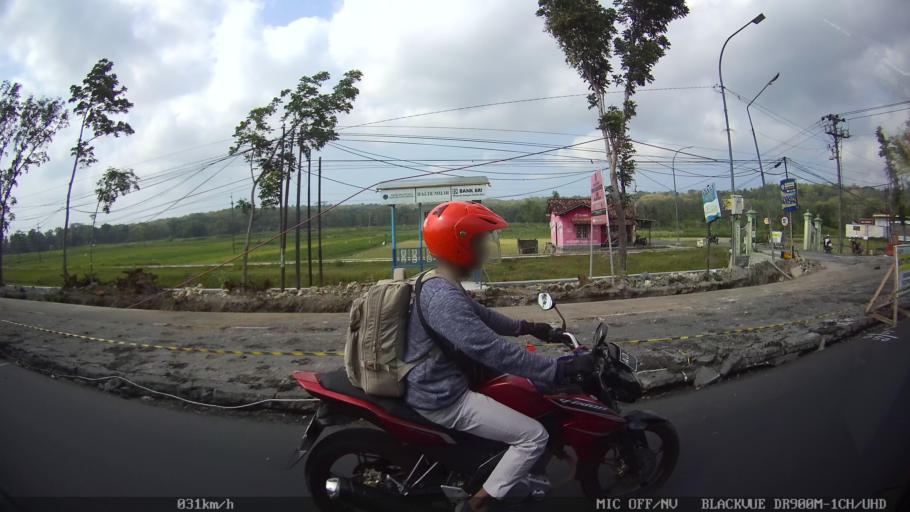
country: ID
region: Daerah Istimewa Yogyakarta
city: Srandakan
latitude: -7.8687
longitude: 110.1905
